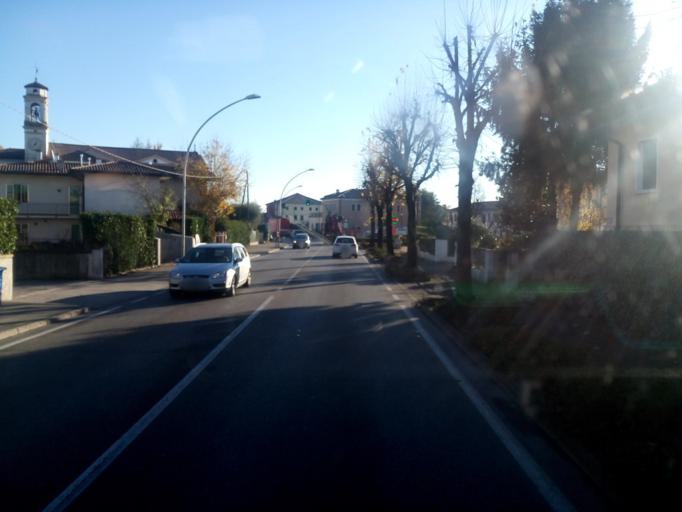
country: IT
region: Veneto
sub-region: Provincia di Vicenza
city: Rossano Veneto
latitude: 45.6965
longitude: 11.8301
